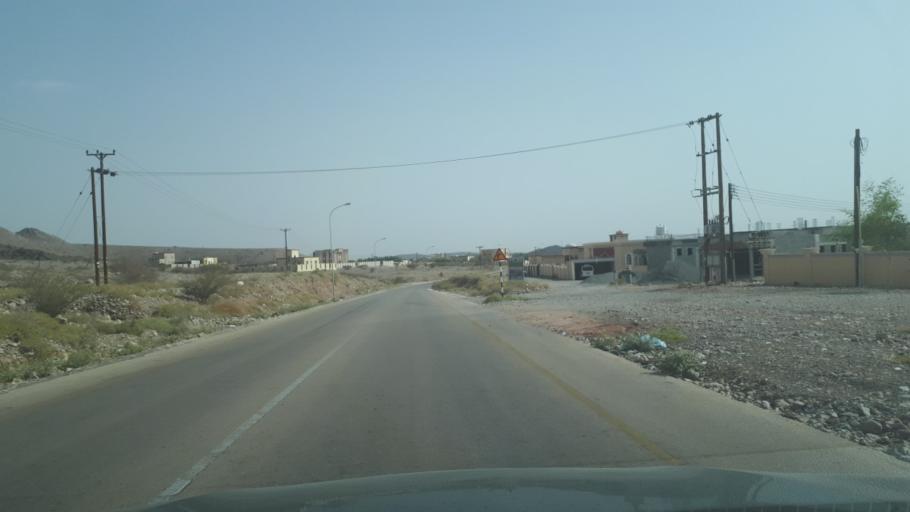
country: OM
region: Az Zahirah
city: `Ibri
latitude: 23.1675
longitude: 56.9165
